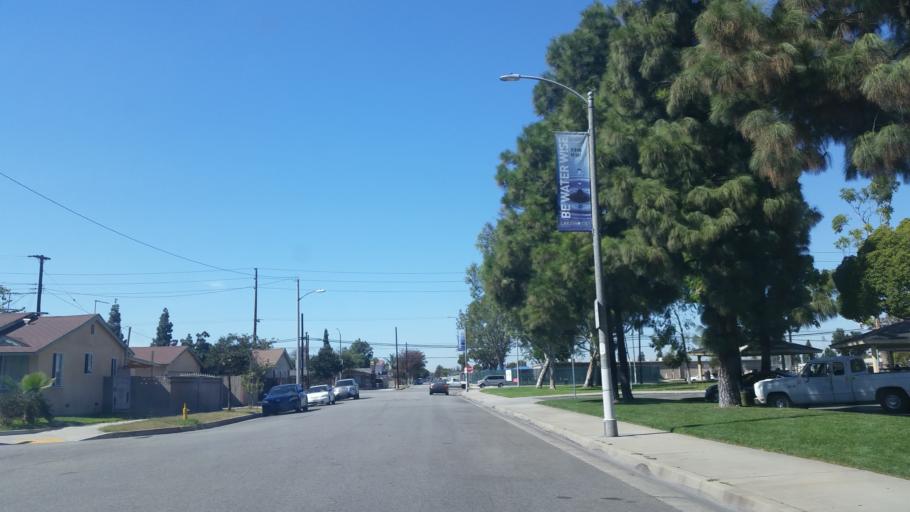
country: US
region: California
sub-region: Los Angeles County
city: Hawaiian Gardens
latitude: 33.8424
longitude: -118.0708
